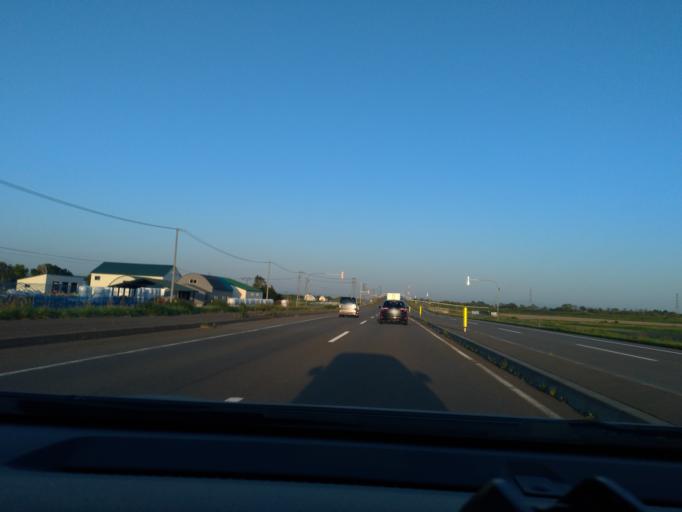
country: JP
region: Hokkaido
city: Tobetsu
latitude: 43.1807
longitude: 141.4818
